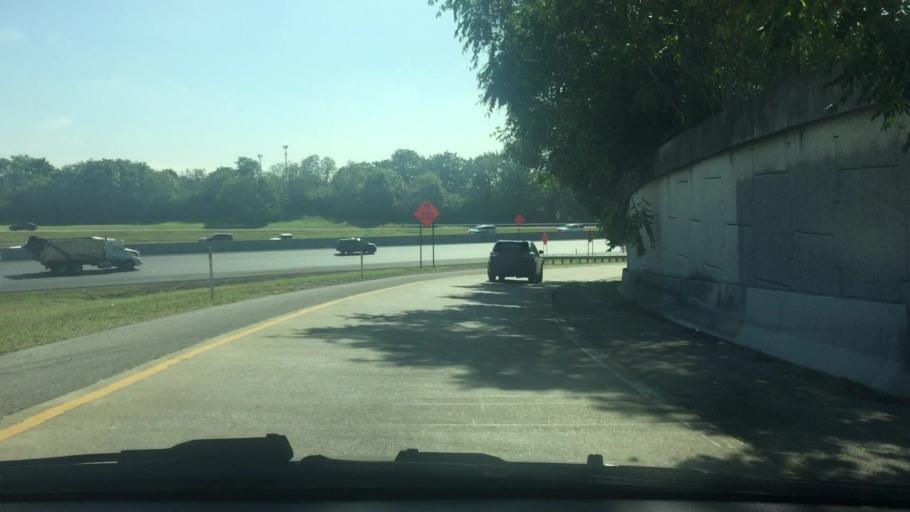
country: US
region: Tennessee
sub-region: Davidson County
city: Oak Hill
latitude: 36.0810
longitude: -86.7653
